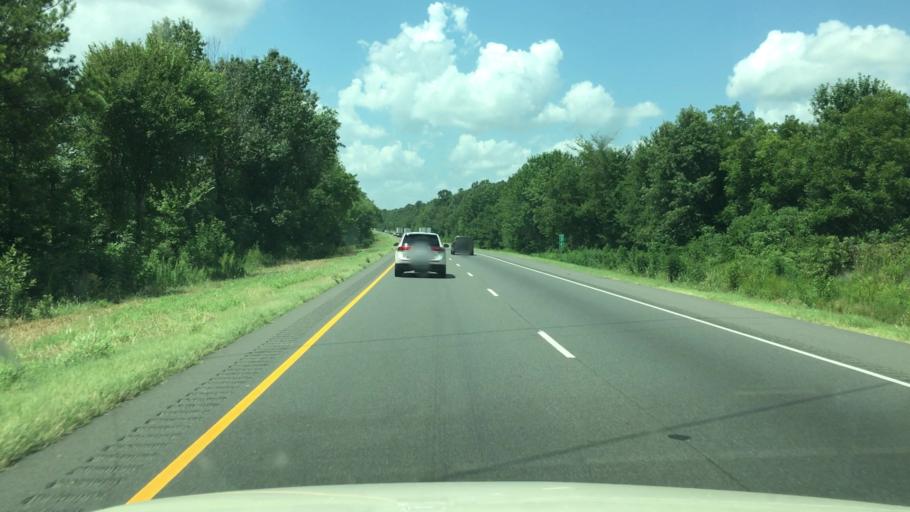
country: US
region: Arkansas
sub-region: Hempstead County
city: Hope
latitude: 33.7205
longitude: -93.5564
